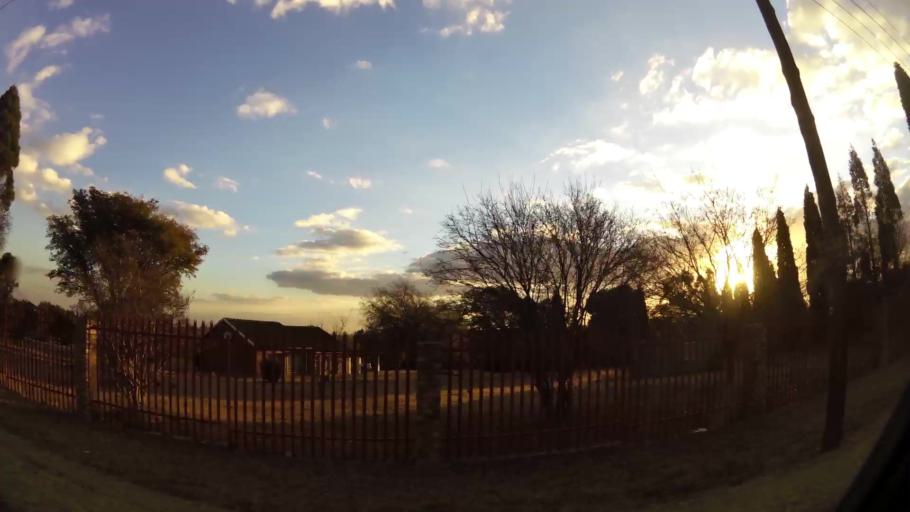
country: ZA
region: Gauteng
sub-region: City of Johannesburg Metropolitan Municipality
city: Midrand
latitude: -26.0030
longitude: 28.1519
